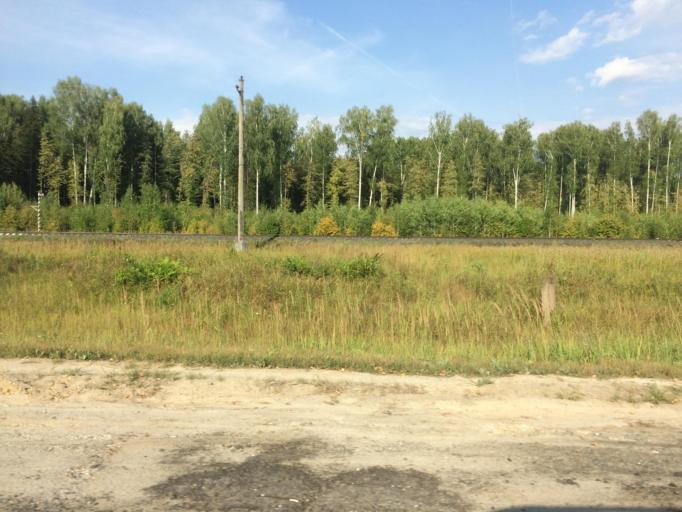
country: RU
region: Mariy-El
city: Yoshkar-Ola
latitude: 56.5596
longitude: 47.9804
